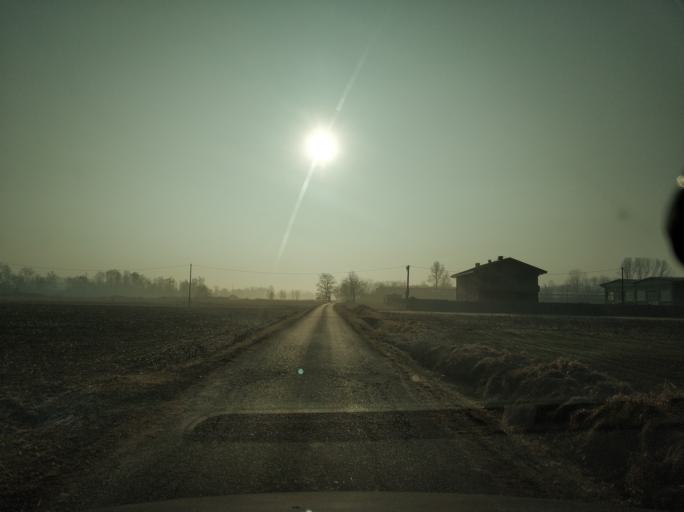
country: IT
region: Piedmont
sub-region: Provincia di Torino
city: Rivarossa
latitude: 45.2551
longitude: 7.7236
